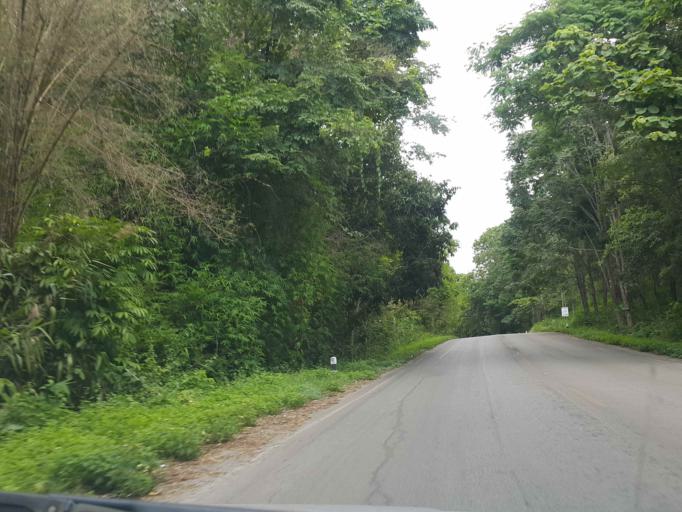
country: TH
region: Chiang Mai
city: Hang Dong
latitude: 18.7821
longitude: 98.8480
